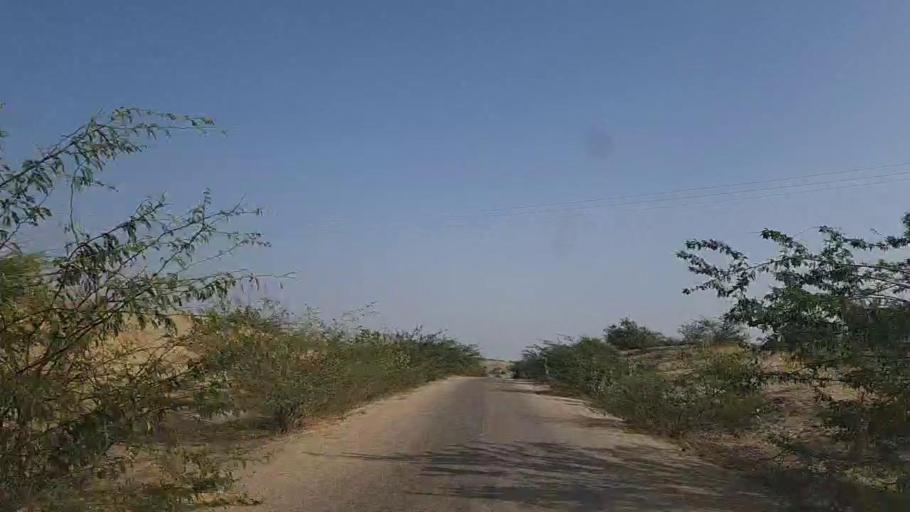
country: PK
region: Sindh
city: Naukot
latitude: 24.6242
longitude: 69.3686
